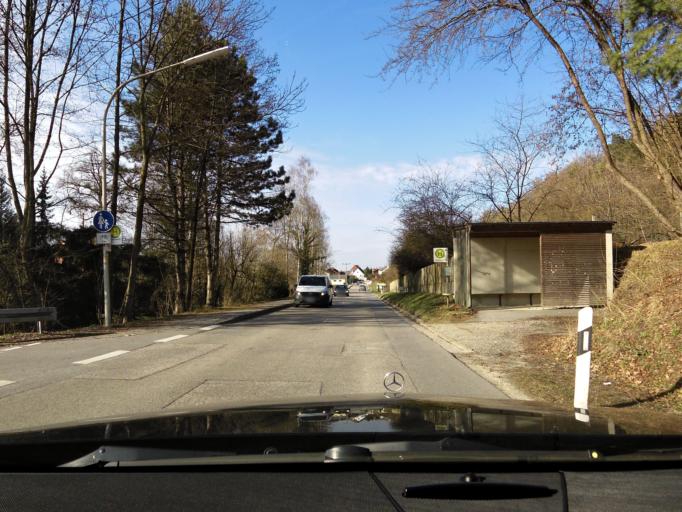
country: DE
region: Bavaria
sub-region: Lower Bavaria
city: Tiefenbach
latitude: 48.5059
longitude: 12.0990
